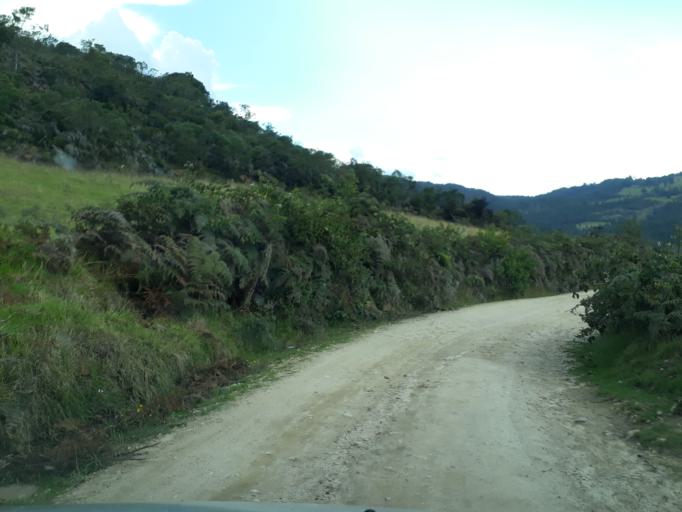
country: CO
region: Cundinamarca
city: Lenguazaque
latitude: 5.2597
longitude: -73.6891
